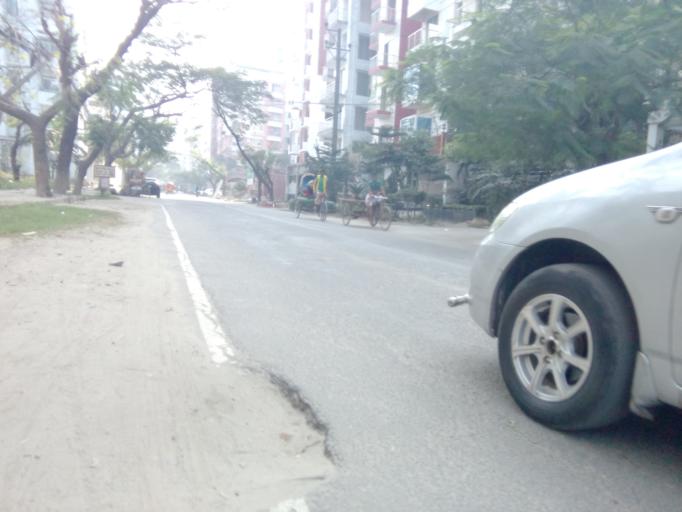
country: BD
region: Dhaka
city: Tungi
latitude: 23.8199
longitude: 90.4339
